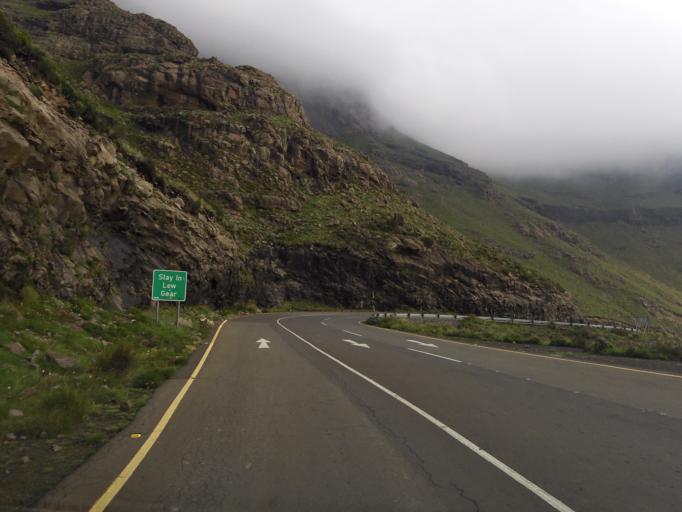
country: LS
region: Butha-Buthe
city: Butha-Buthe
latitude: -29.0660
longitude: 28.3945
